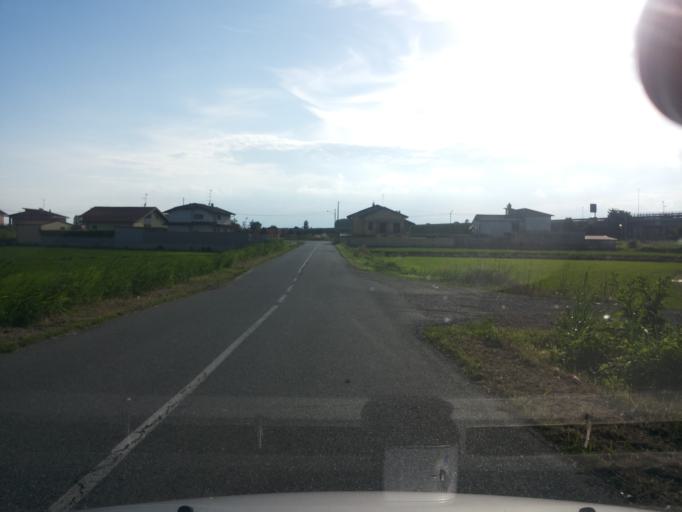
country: IT
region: Piedmont
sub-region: Provincia di Vercelli
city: Borgo Vercelli
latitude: 45.3631
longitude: 8.4626
